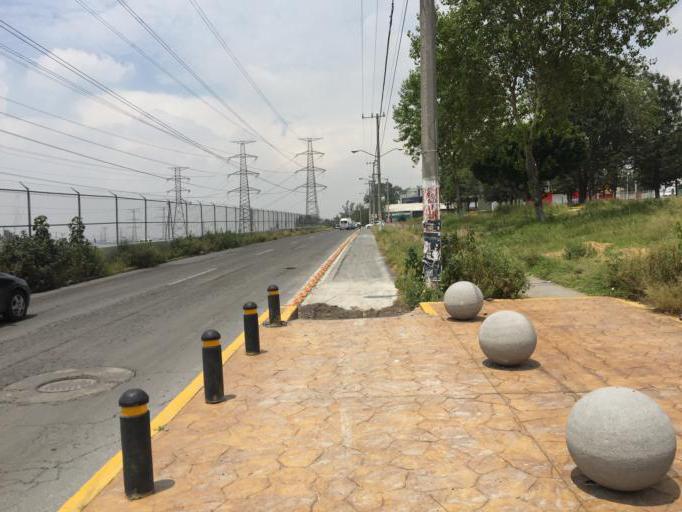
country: MX
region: Mexico
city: Cuautitlan Izcalli
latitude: 19.6359
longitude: -99.2048
